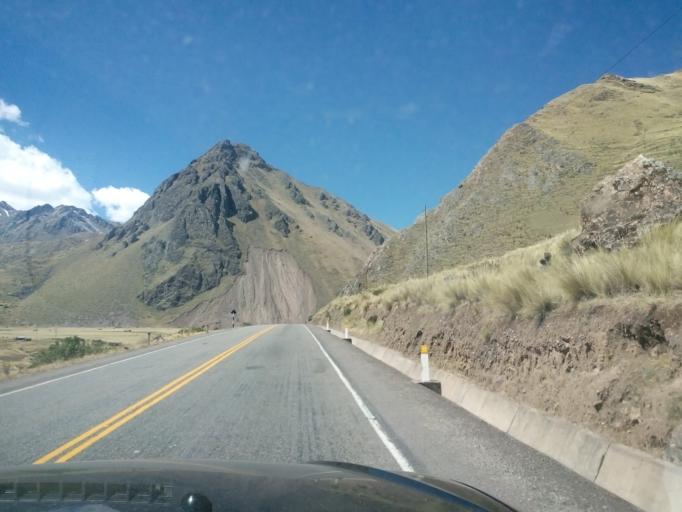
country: PE
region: Cusco
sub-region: Provincia de Canas
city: Layo
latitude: -14.4498
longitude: -71.0799
